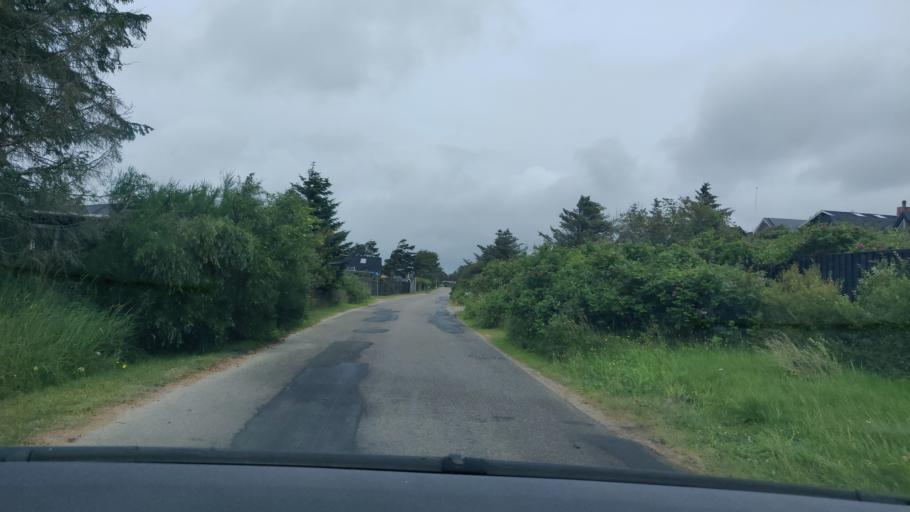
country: DK
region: North Denmark
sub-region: Jammerbugt Kommune
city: Pandrup
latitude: 57.2558
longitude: 9.5950
